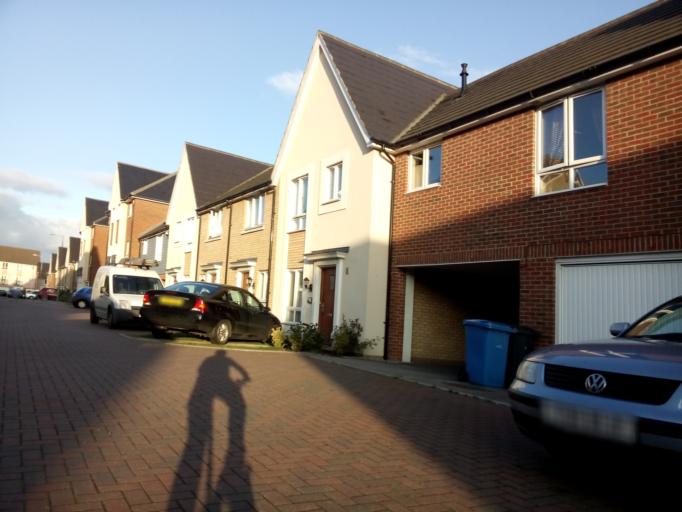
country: GB
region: England
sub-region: Suffolk
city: Bramford
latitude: 52.0668
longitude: 1.1180
